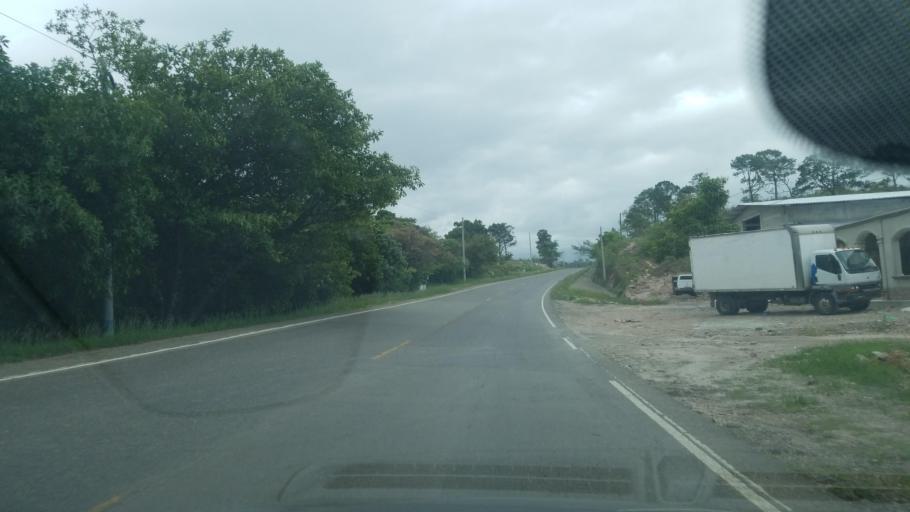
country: HN
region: Ocotepeque
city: Lucerna
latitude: 14.5525
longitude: -88.9414
